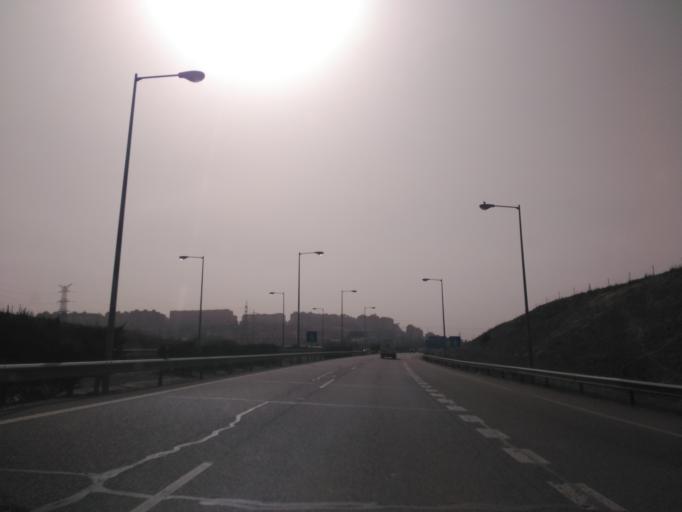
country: ES
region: Castille and Leon
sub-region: Provincia de Valladolid
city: Zaratan
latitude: 41.6486
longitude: -4.7654
